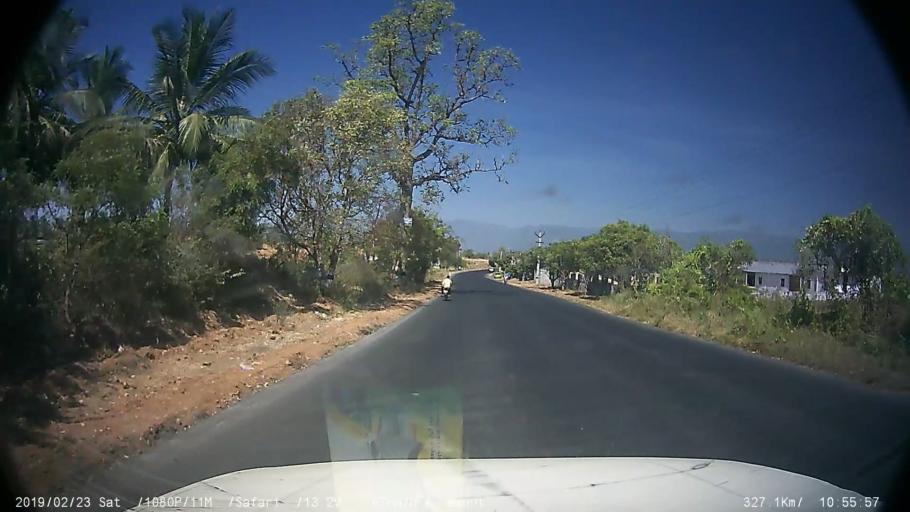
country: IN
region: Tamil Nadu
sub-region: Coimbatore
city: Sirumugai
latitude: 11.2595
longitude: 77.0341
